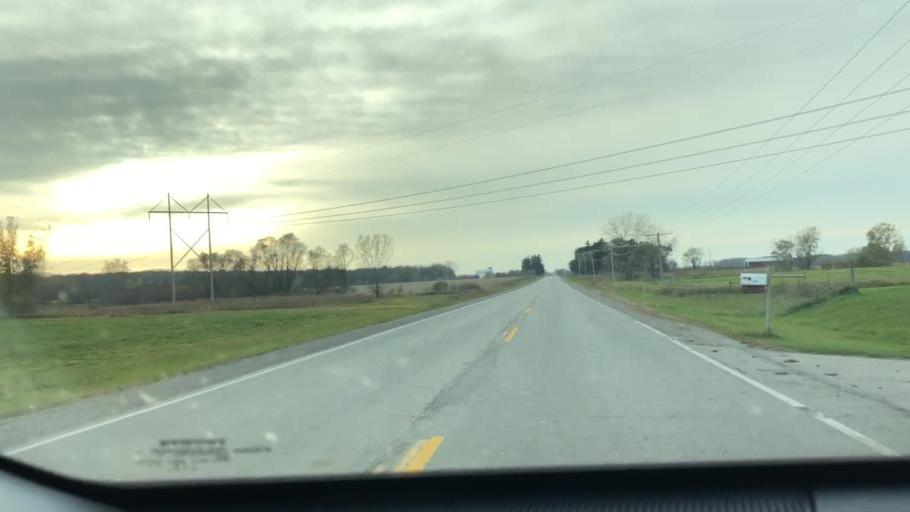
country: US
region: Wisconsin
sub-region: Outagamie County
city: Seymour
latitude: 44.4437
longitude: -88.3121
